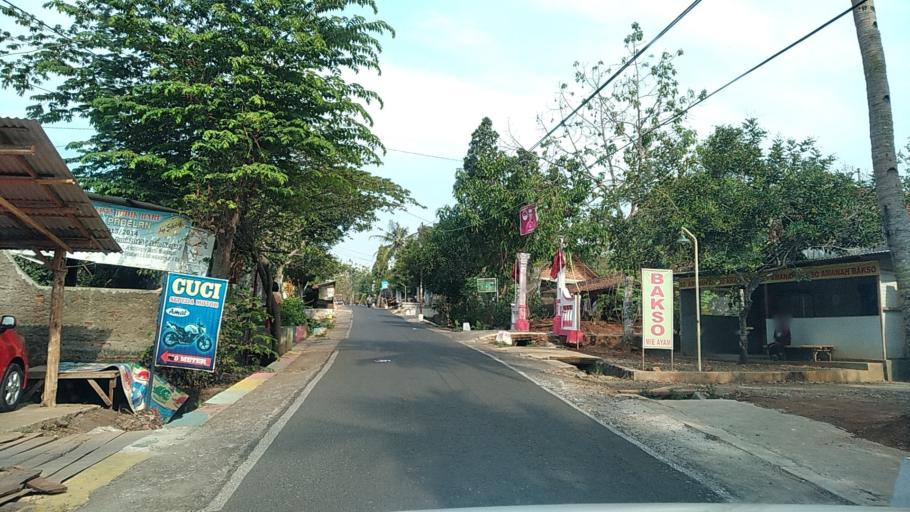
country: ID
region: Central Java
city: Semarang
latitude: -7.0405
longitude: 110.3040
